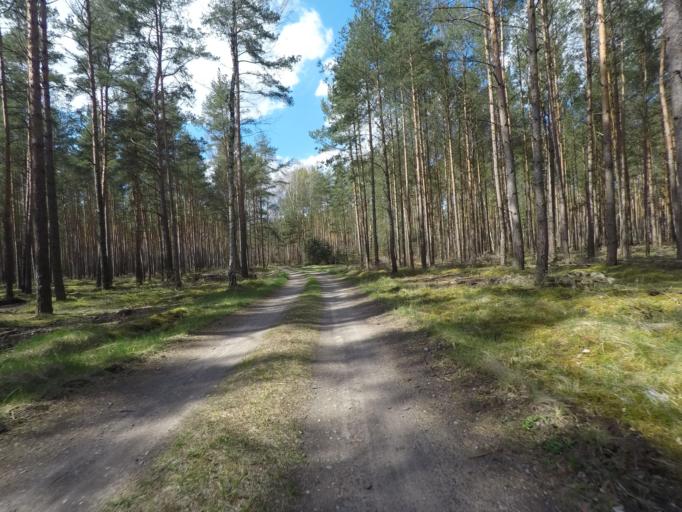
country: DE
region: Brandenburg
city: Melchow
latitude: 52.8197
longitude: 13.6885
